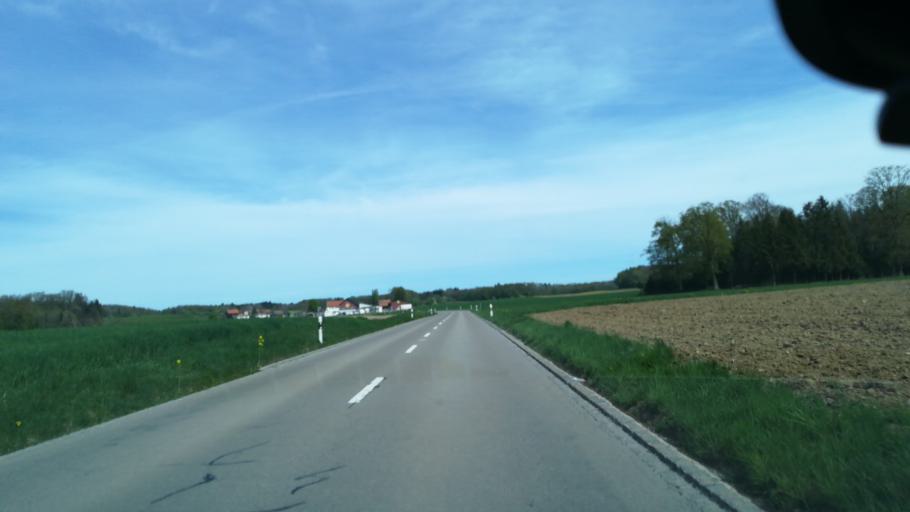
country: CH
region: Thurgau
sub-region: Weinfelden District
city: Maerstetten-Dorf
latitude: 47.6318
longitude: 9.0683
